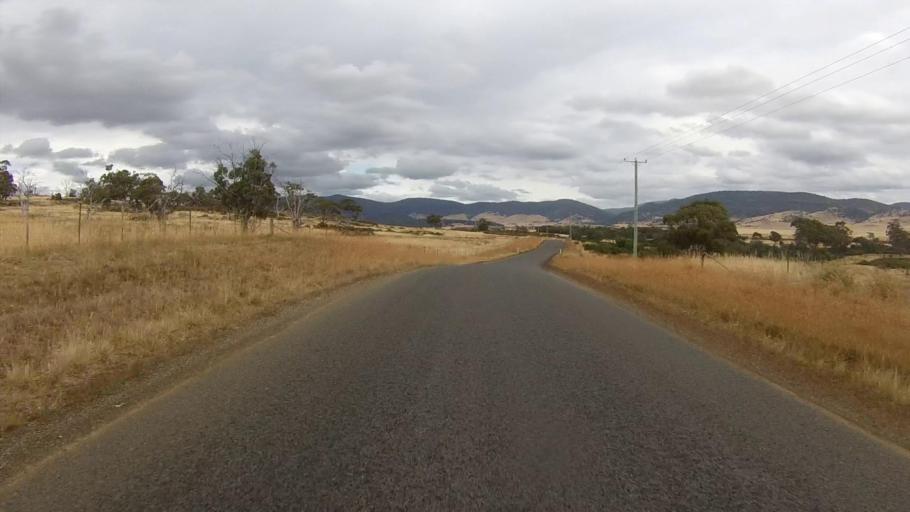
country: AU
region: Tasmania
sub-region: Northern Midlands
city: Evandale
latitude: -41.8080
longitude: 147.7534
